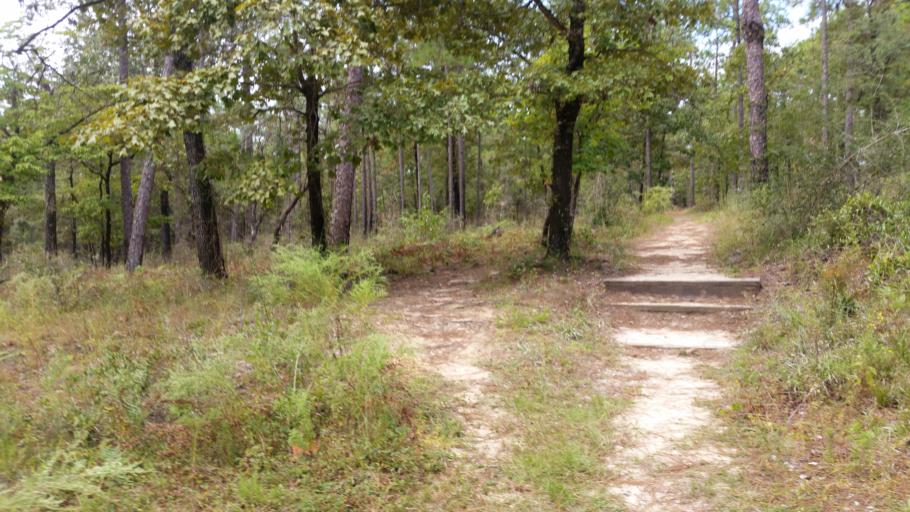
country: US
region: Florida
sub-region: Santa Rosa County
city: Point Baker
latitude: 30.8620
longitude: -86.8445
